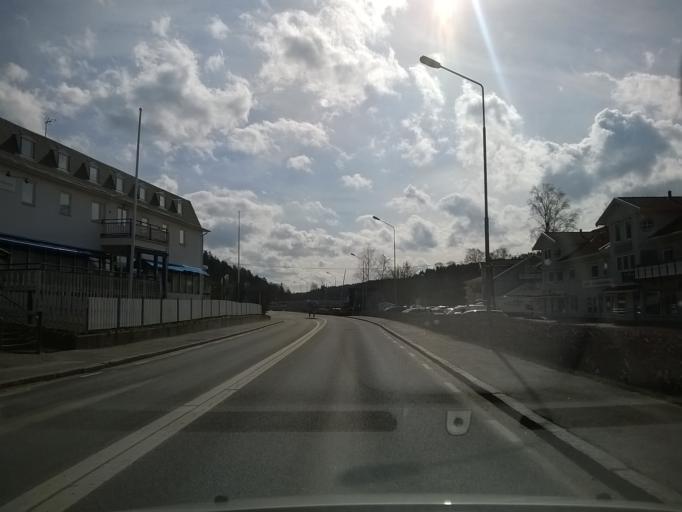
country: SE
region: Vaestra Goetaland
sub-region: Orust
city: Henan
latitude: 58.2380
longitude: 11.6803
